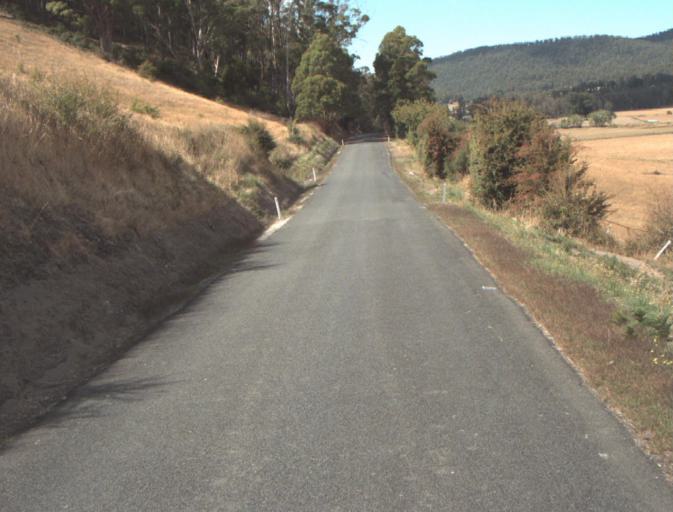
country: AU
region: Tasmania
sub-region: Launceston
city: Mayfield
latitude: -41.2423
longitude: 147.1499
